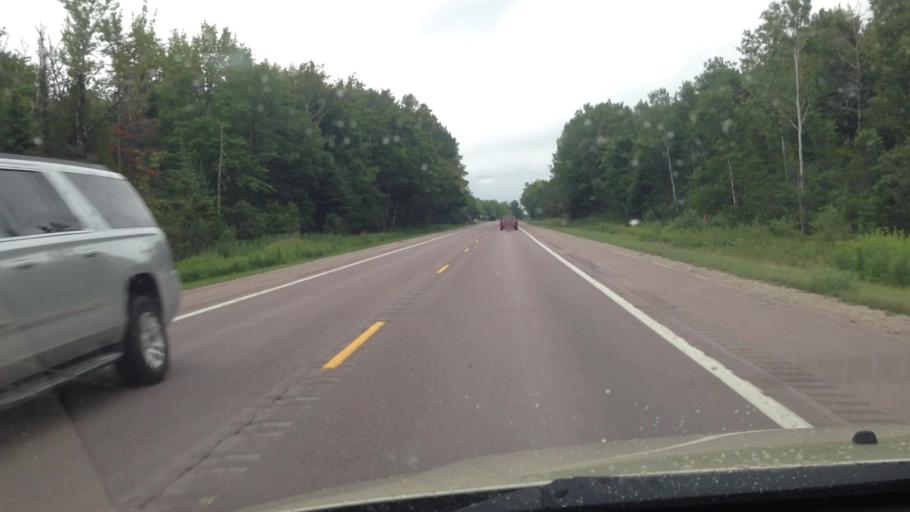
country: US
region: Michigan
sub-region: Schoolcraft County
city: Manistique
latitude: 45.9774
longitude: -86.1412
